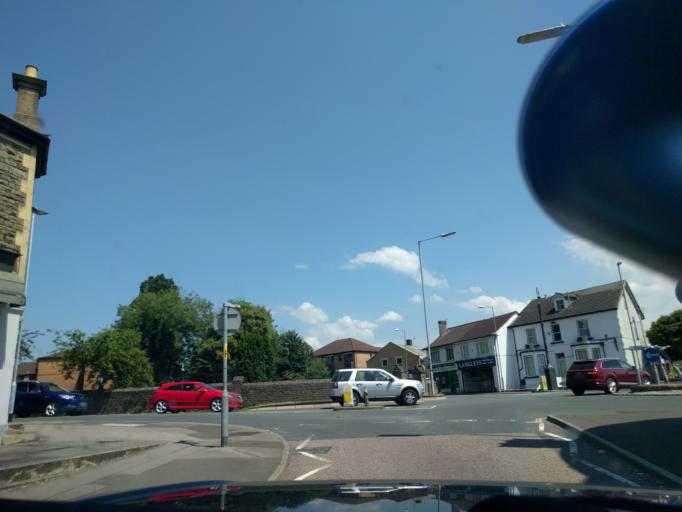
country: GB
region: England
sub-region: Wiltshire
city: Chippenham
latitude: 51.4638
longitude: -2.1176
